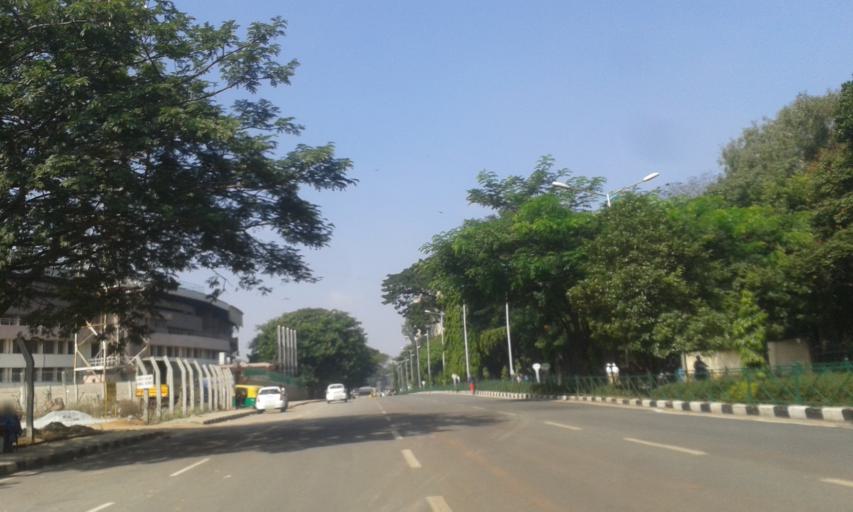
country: IN
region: Karnataka
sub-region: Bangalore Urban
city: Bangalore
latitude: 12.9795
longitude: 77.6015
